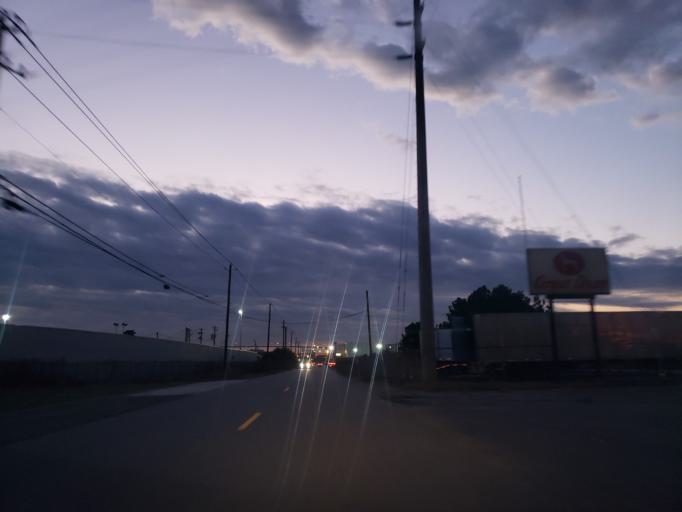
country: US
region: Georgia
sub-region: Chatham County
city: Savannah
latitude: 32.0969
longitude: -81.1166
